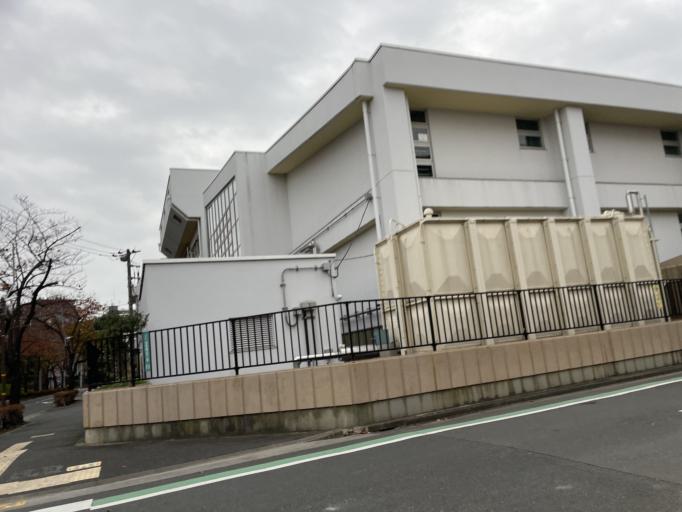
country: JP
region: Tokyo
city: Urayasu
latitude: 35.6751
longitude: 139.8651
